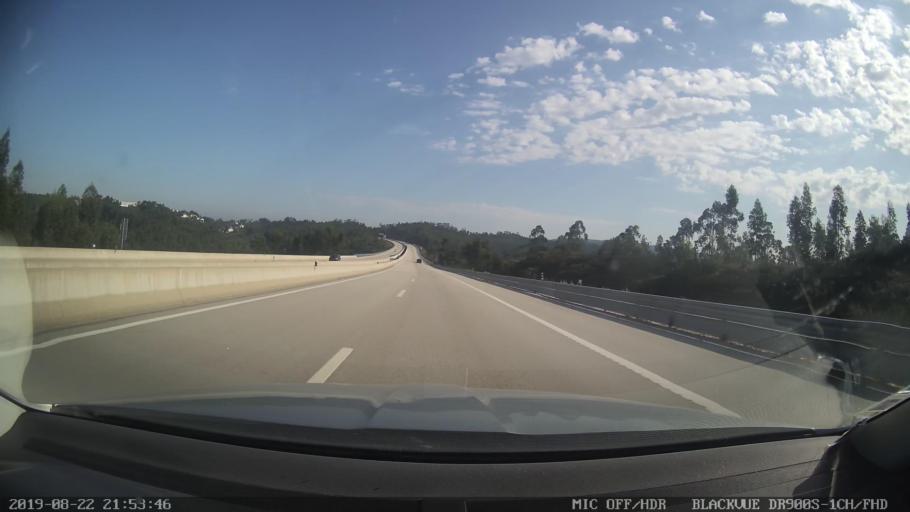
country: PT
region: Coimbra
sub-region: Miranda do Corvo
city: Miranda do Corvo
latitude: 40.1210
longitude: -8.3839
